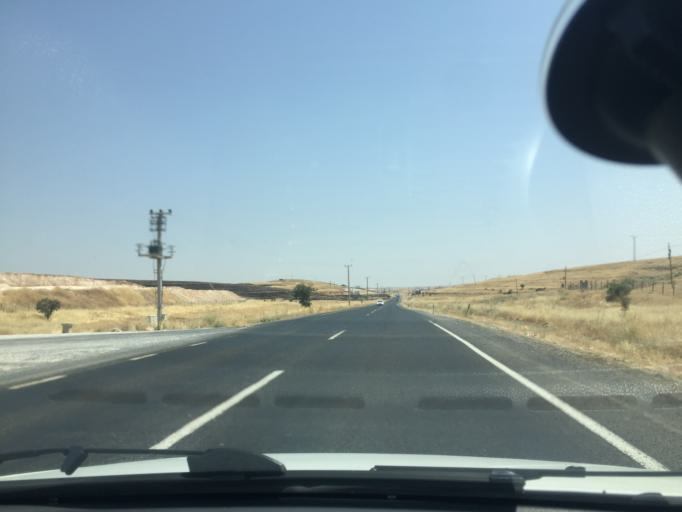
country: TR
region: Mardin
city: Kindirip
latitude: 37.4621
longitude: 41.2318
